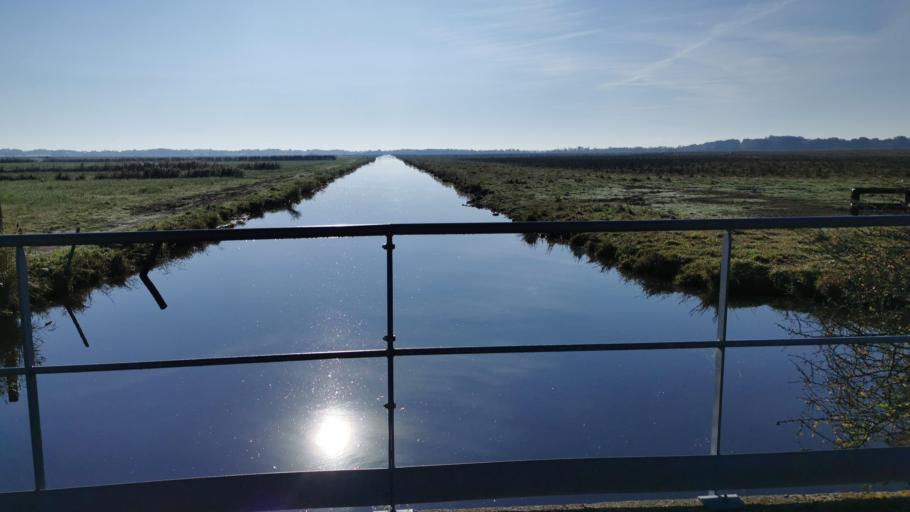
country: FR
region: Pays de la Loire
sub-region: Departement de la Loire-Atlantique
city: Crossac
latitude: 47.3881
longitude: -2.1640
